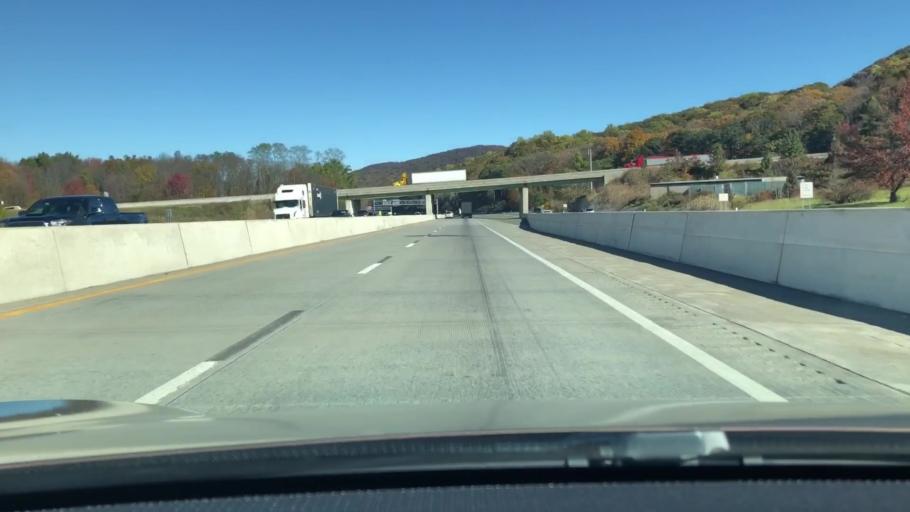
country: US
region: New York
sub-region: Orange County
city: Harriman
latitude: 41.3099
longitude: -74.1238
